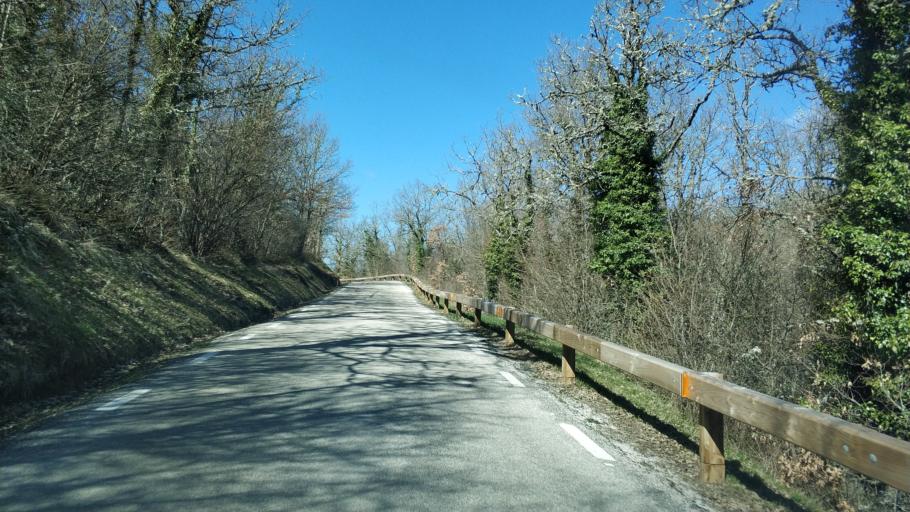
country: ES
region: Cantabria
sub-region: Provincia de Cantabria
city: Mataporquera
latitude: 42.8700
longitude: -4.0732
